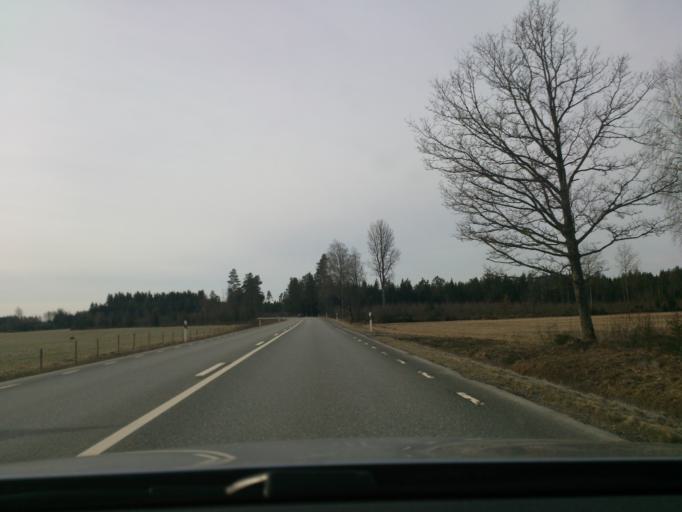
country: SE
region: Kronoberg
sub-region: Alvesta Kommun
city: Moheda
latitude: 56.9527
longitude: 14.5665
